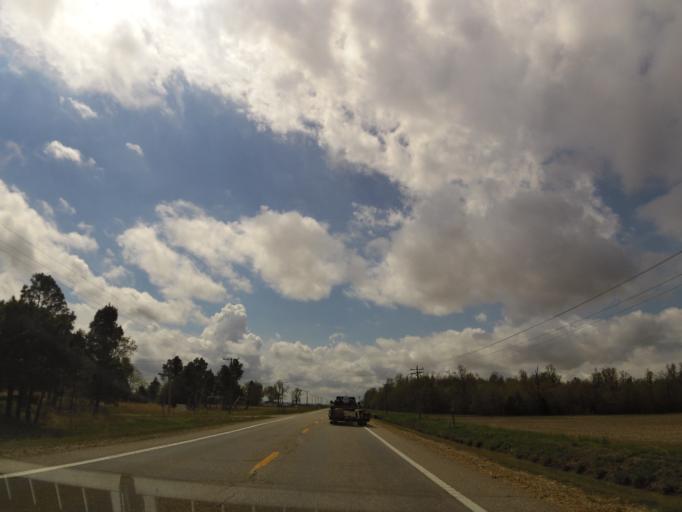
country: US
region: Arkansas
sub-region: Clay County
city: Corning
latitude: 36.3404
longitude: -90.5253
